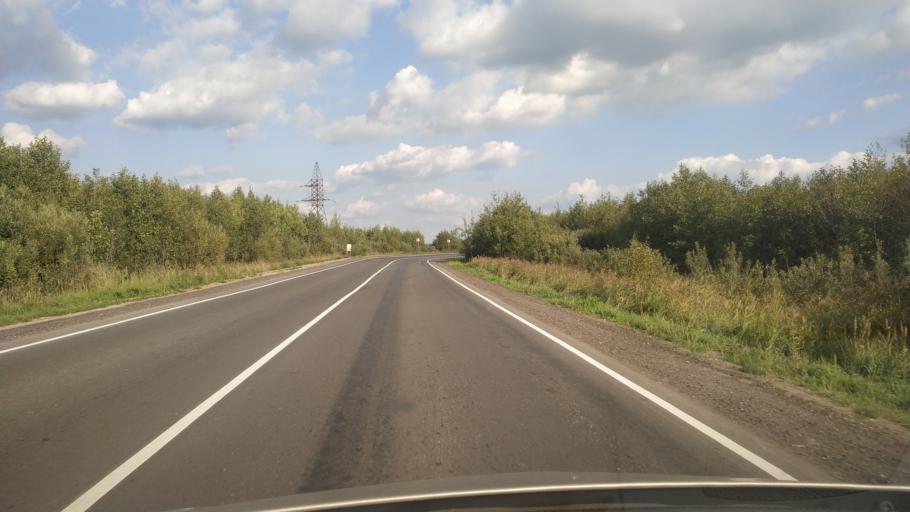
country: RU
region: Moskovskaya
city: Vereya
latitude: 55.7255
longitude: 39.0450
